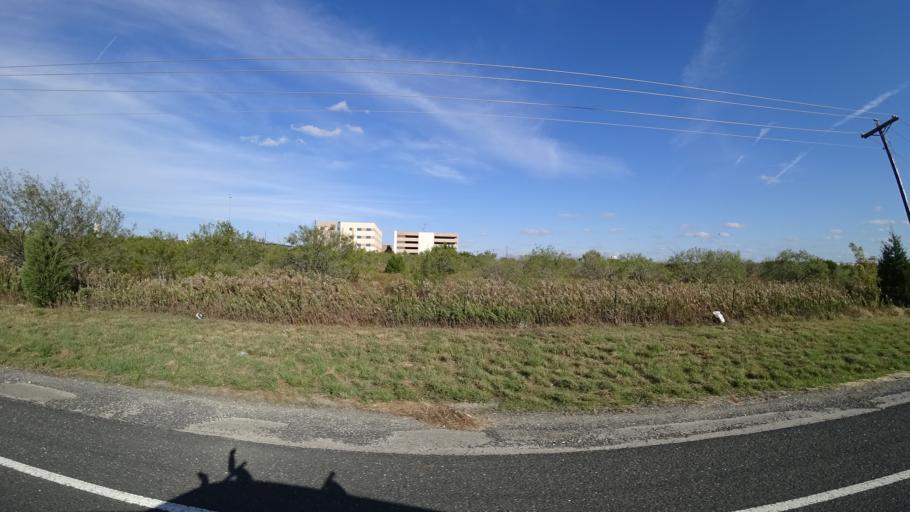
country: US
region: Texas
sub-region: Travis County
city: Wells Branch
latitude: 30.4757
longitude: -97.6934
